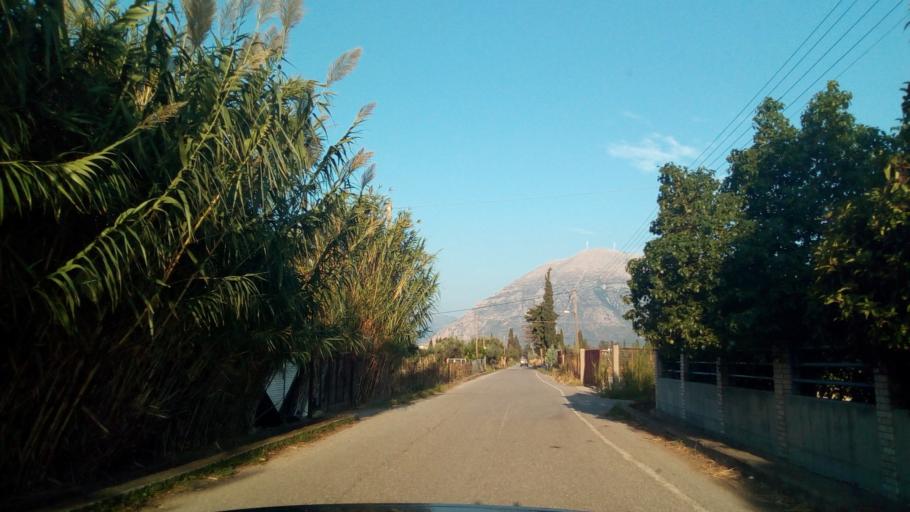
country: GR
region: West Greece
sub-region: Nomos Aitolias kai Akarnanias
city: Antirrio
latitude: 38.3347
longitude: 21.7536
